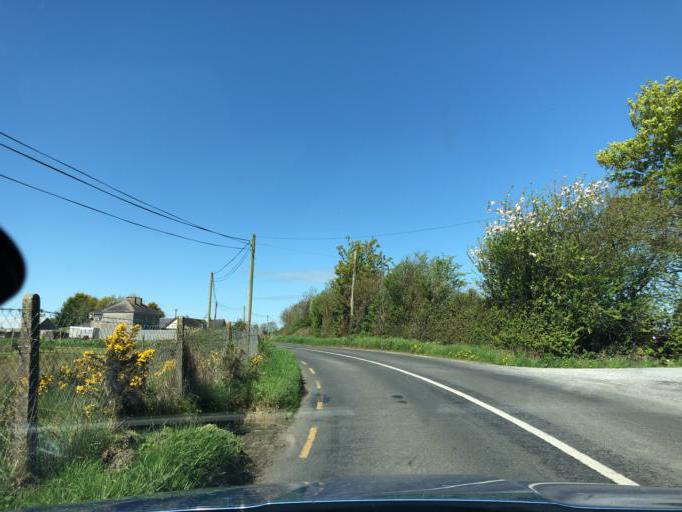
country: IE
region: Connaught
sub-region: County Galway
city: Portumna
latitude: 53.1256
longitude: -8.3353
